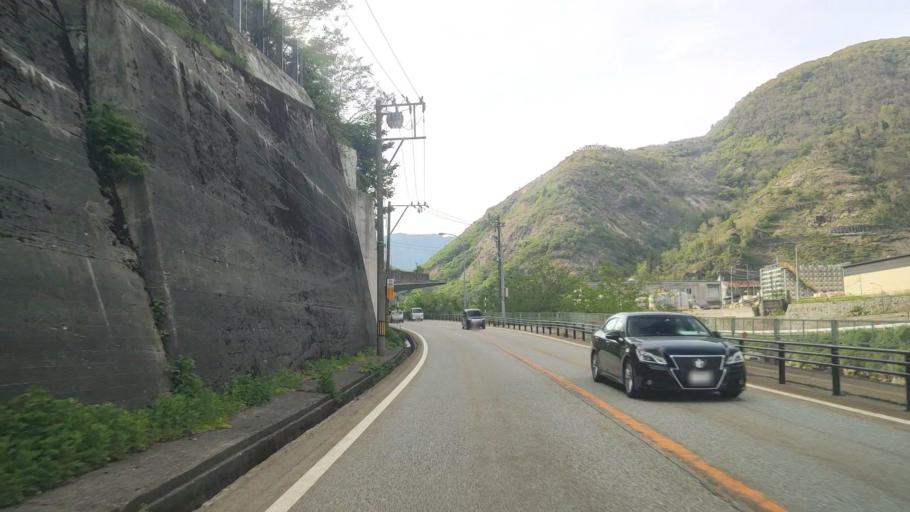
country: JP
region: Gifu
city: Takayama
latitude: 36.3468
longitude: 137.2939
